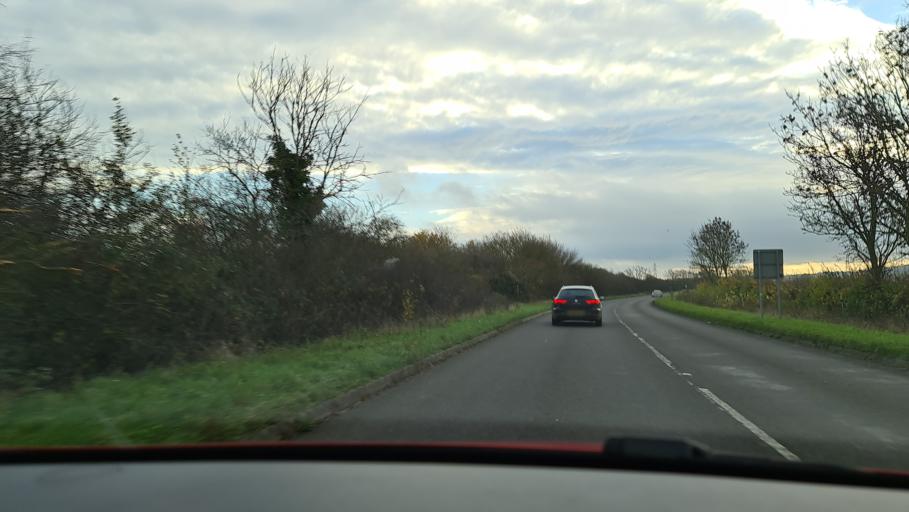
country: GB
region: England
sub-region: Oxfordshire
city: Bicester
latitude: 51.8668
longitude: -1.0973
